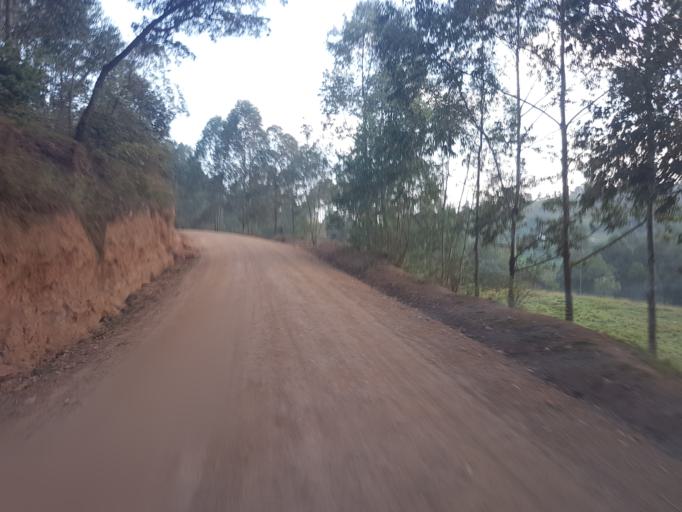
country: UG
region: Western Region
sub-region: Rukungiri District
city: Rukungiri
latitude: -0.7489
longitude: 29.9301
